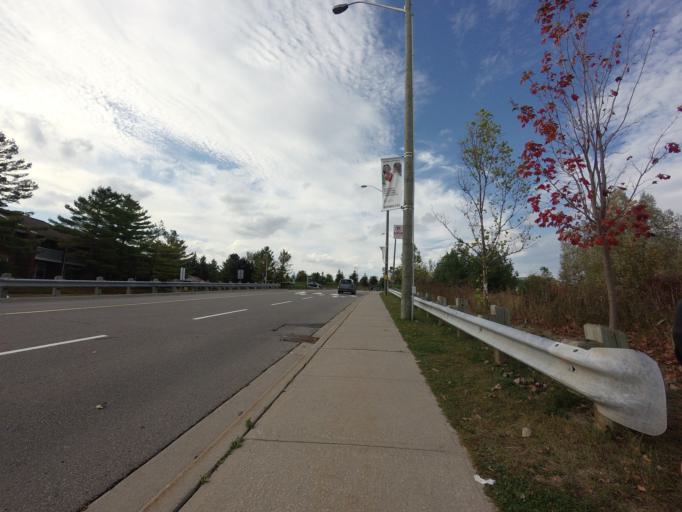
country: CA
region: Ontario
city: Mississauga
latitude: 43.5461
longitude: -79.6606
